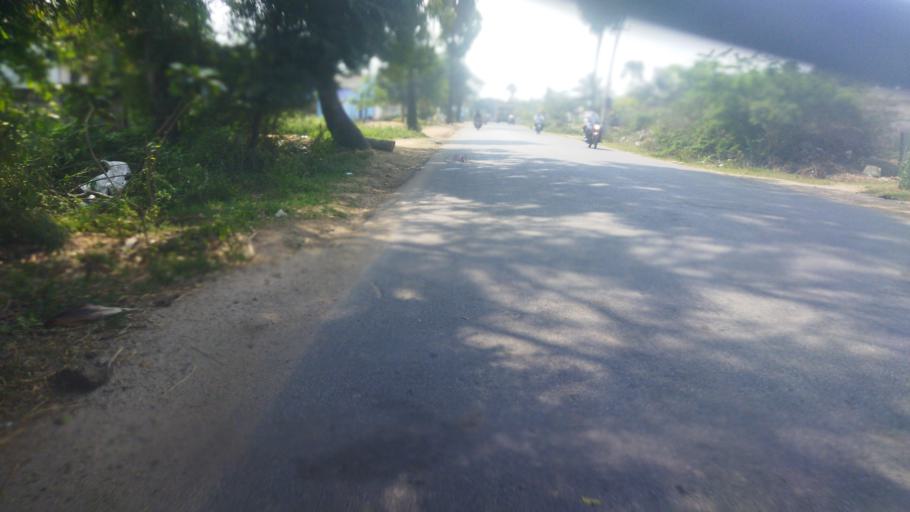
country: IN
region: Telangana
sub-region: Nalgonda
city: Nalgonda
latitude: 17.1489
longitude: 79.3103
